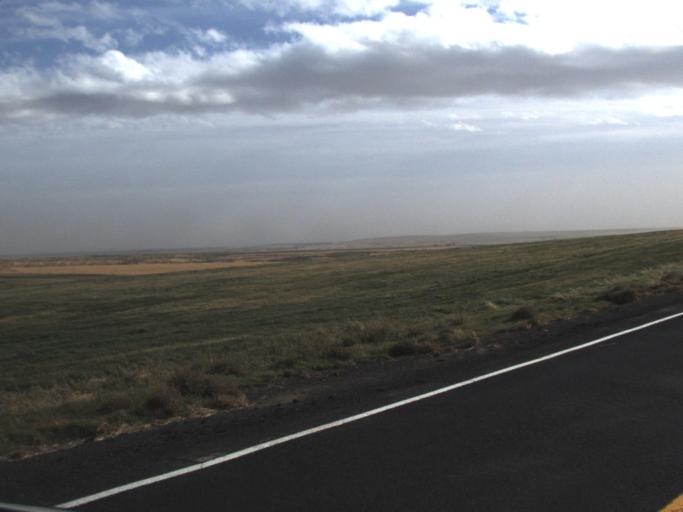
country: US
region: Washington
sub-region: Okanogan County
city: Coulee Dam
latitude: 47.5849
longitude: -118.7860
